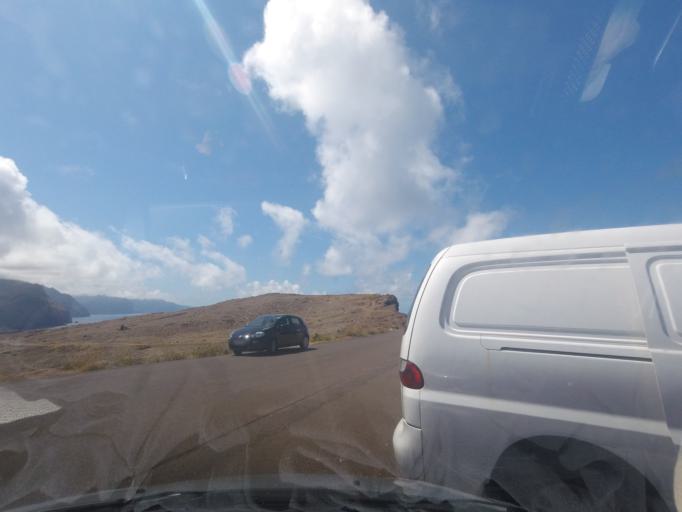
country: PT
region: Madeira
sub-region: Machico
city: Canical
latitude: 32.7491
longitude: -16.7067
